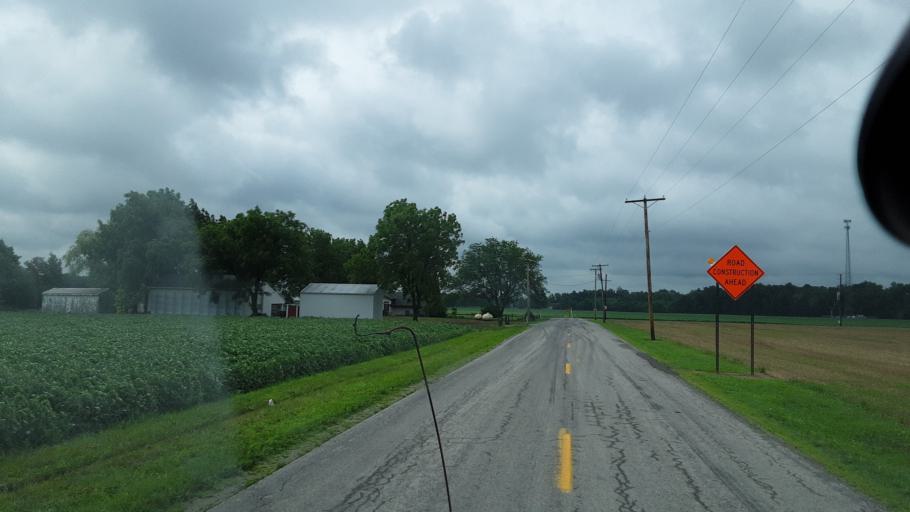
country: US
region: Indiana
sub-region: Allen County
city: Monroeville
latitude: 40.9504
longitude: -84.9686
